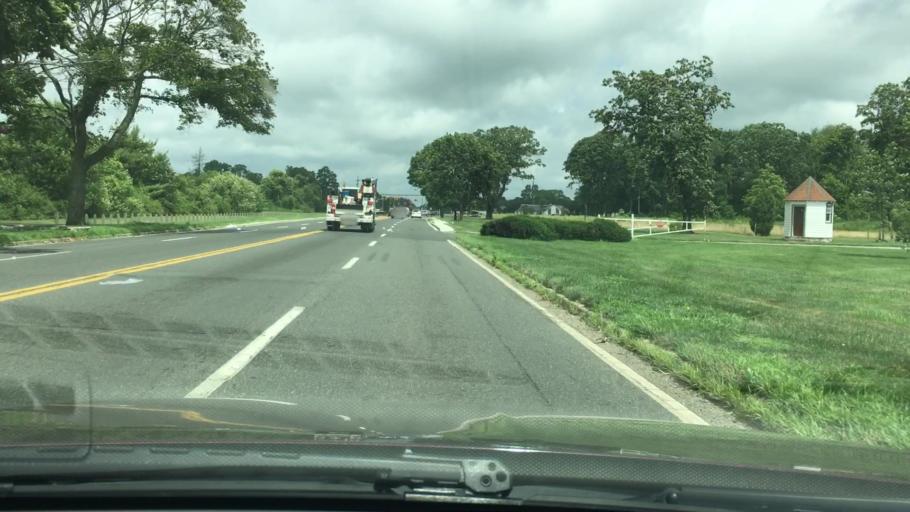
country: US
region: New York
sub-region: Suffolk County
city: East Farmingdale
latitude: 40.7420
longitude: -73.4003
